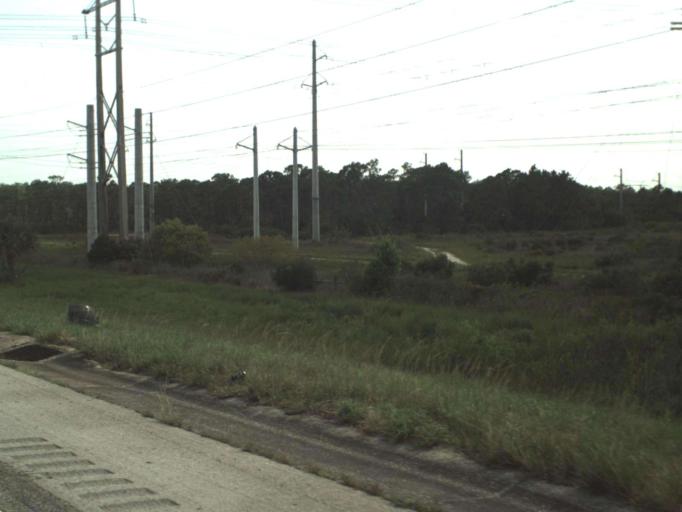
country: US
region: Florida
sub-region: Saint Lucie County
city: River Park
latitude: 27.3509
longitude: -80.4144
